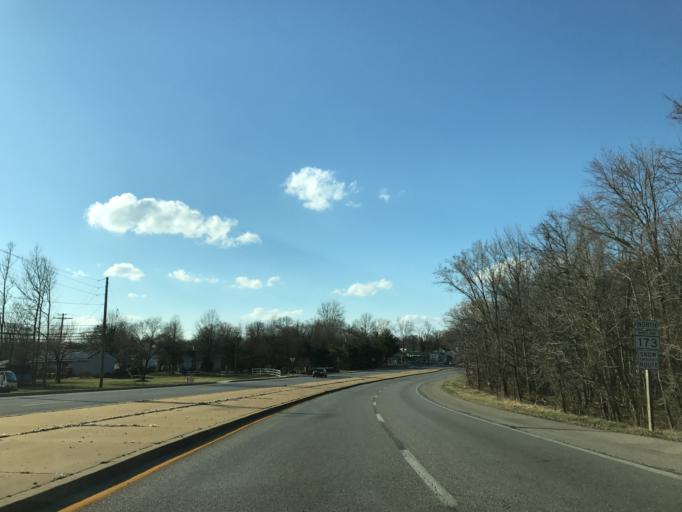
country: US
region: Maryland
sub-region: Anne Arundel County
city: Green Haven
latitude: 39.1816
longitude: -76.5489
